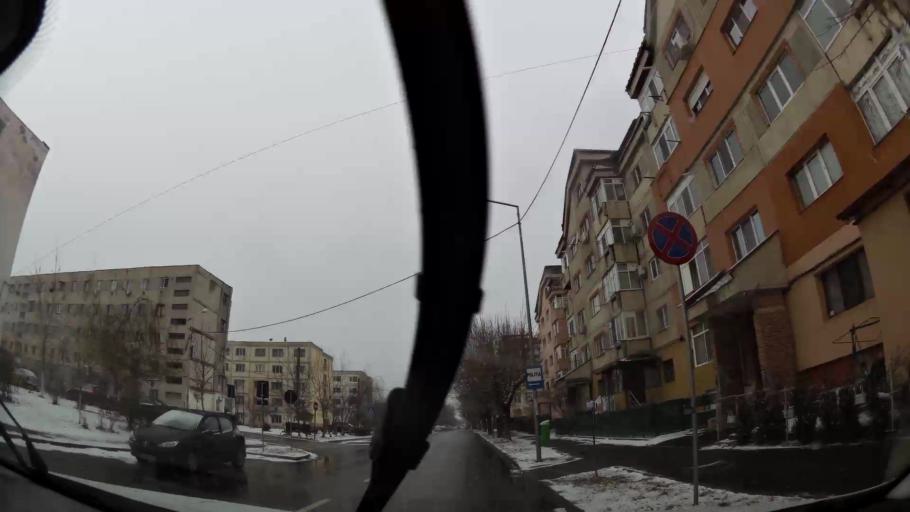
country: RO
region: Dambovita
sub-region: Municipiul Targoviste
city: Targoviste
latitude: 44.9159
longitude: 25.4689
